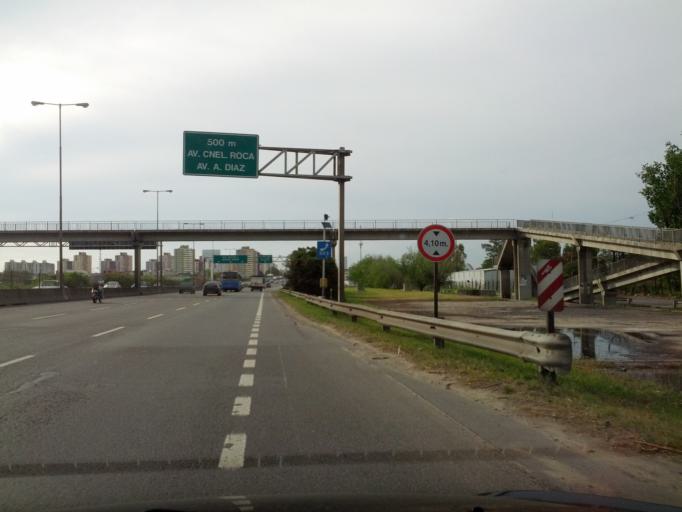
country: AR
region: Buenos Aires F.D.
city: Villa Lugano
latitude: -34.7014
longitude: -58.4659
